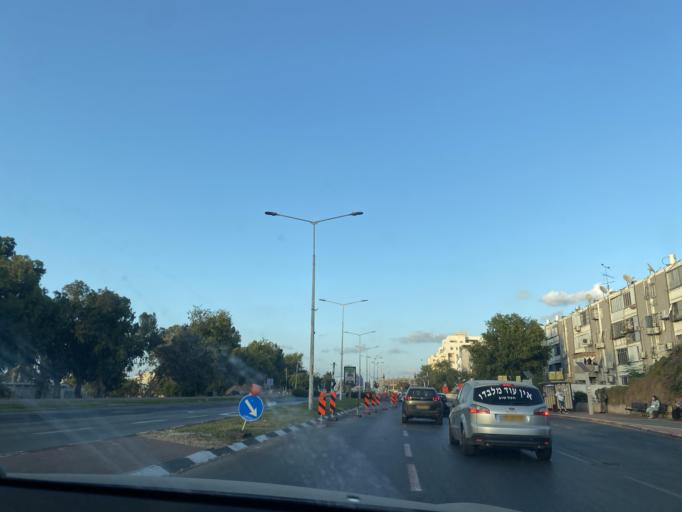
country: IL
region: Southern District
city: Ashdod
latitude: 31.8049
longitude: 34.6606
